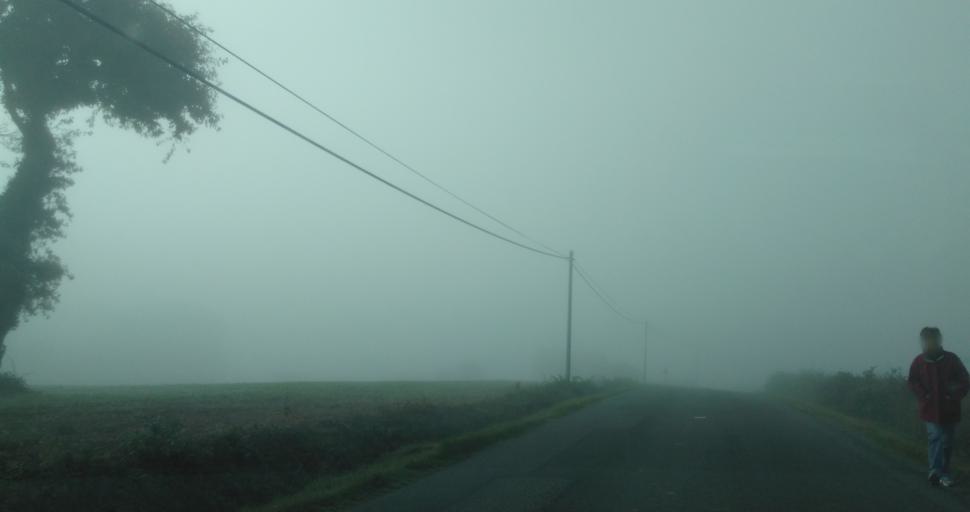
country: FR
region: Brittany
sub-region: Departement d'Ille-et-Vilaine
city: Iffendic
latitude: 48.1401
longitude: -2.0196
